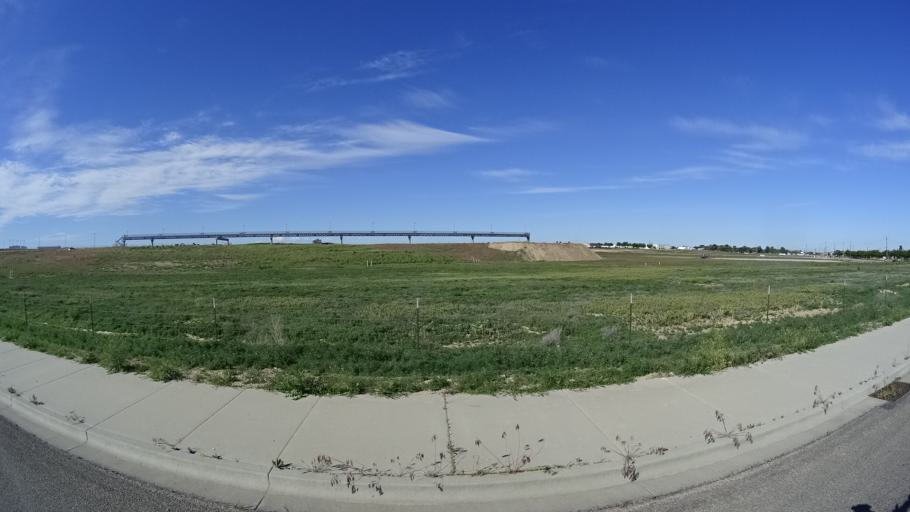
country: US
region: Idaho
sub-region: Ada County
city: Garden City
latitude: 43.5747
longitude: -116.2472
